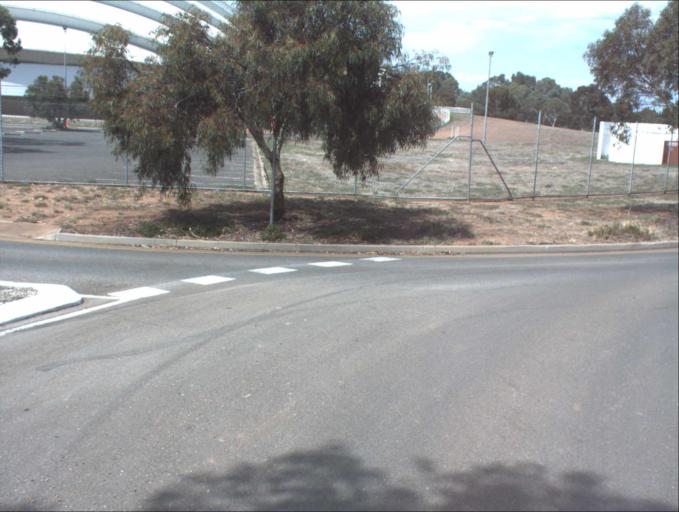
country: AU
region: South Australia
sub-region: Port Adelaide Enfield
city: Enfield
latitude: -34.8399
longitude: 138.6122
